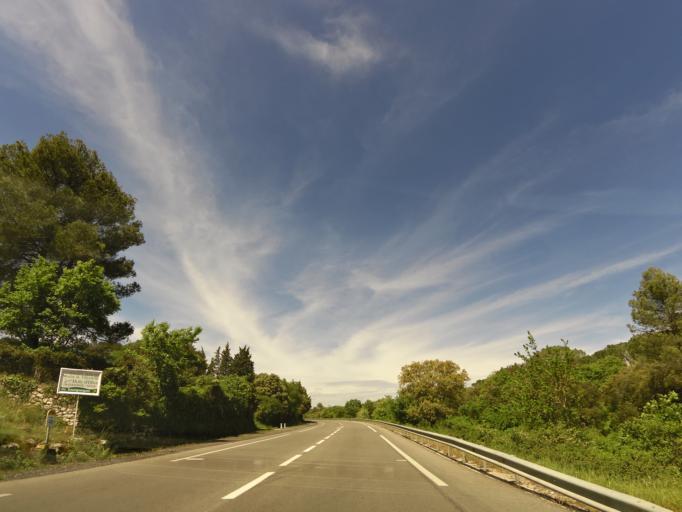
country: FR
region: Languedoc-Roussillon
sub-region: Departement du Gard
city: Villevieille
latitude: 43.7892
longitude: 4.1077
